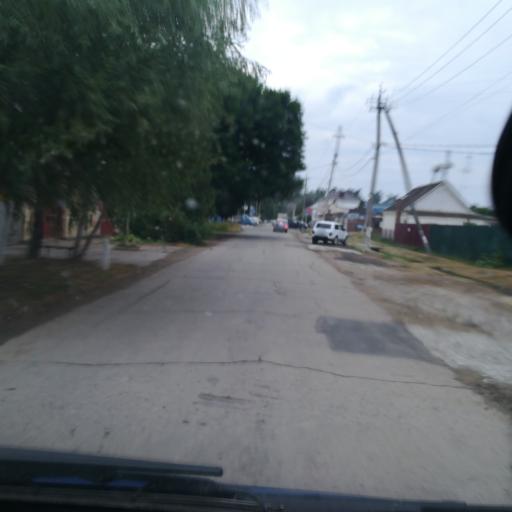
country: RU
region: Krasnodarskiy
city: Slavyansk-na-Kubani
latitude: 45.2630
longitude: 38.1271
